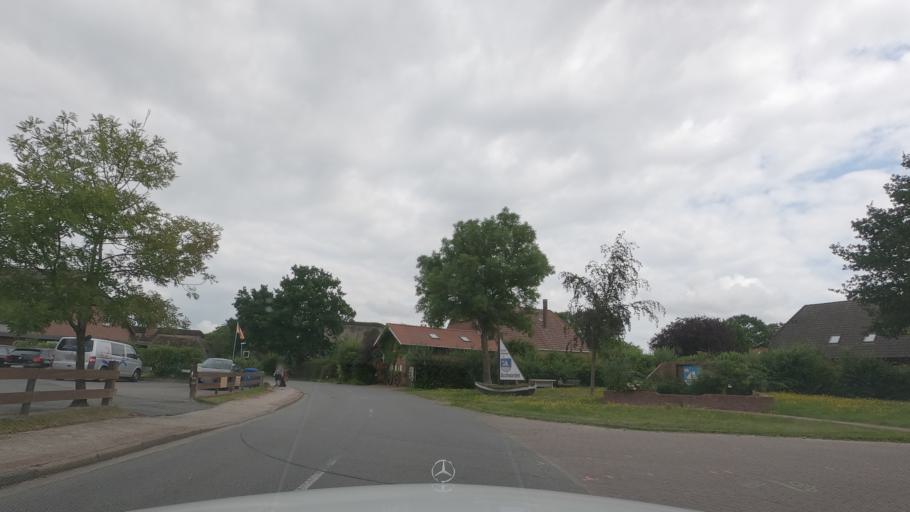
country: DE
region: Lower Saxony
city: Neuenkirchen
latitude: 53.2852
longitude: 8.5333
